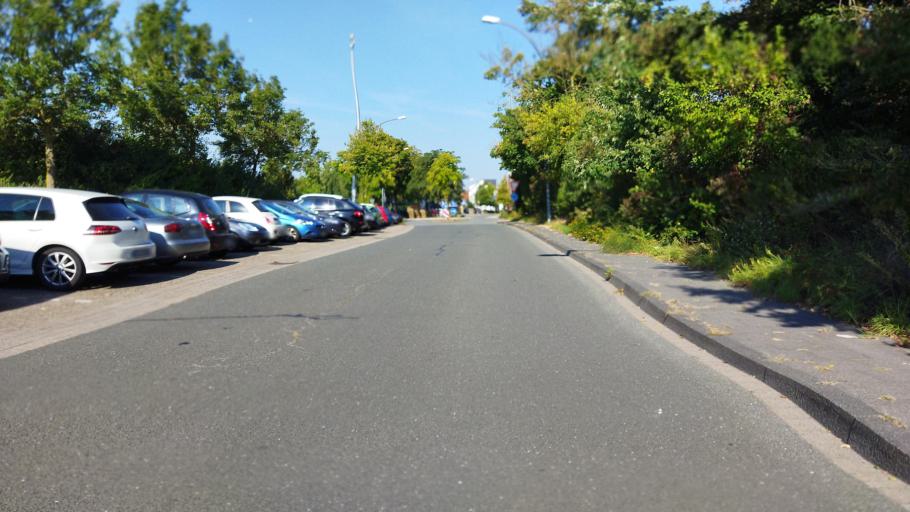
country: DE
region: North Rhine-Westphalia
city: Lengerich
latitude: 52.1749
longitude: 7.8795
